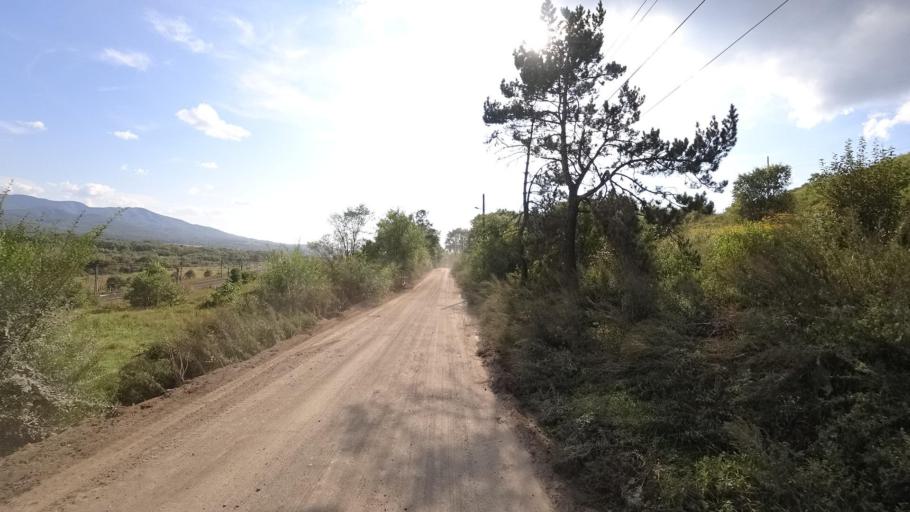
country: RU
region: Jewish Autonomous Oblast
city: Birakan
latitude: 48.9999
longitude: 131.7285
